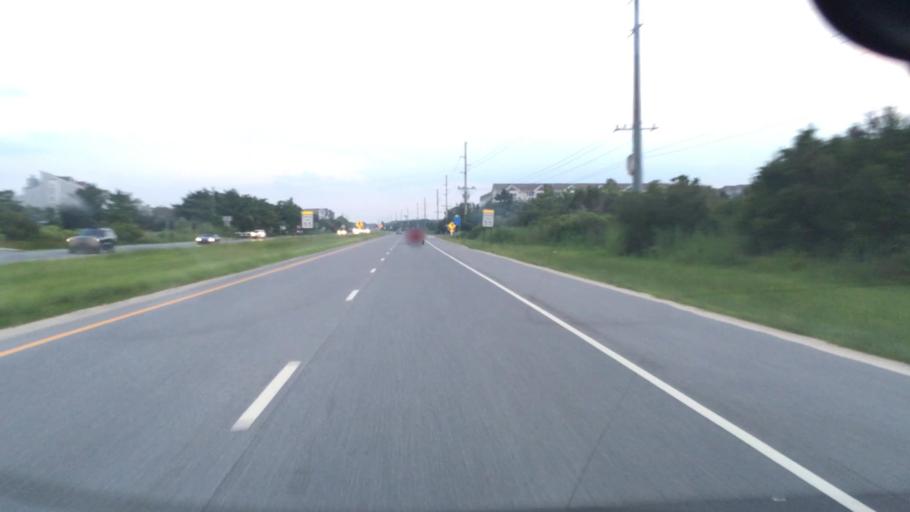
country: US
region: Delaware
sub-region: Sussex County
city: Bethany Beach
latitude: 38.5919
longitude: -75.0622
